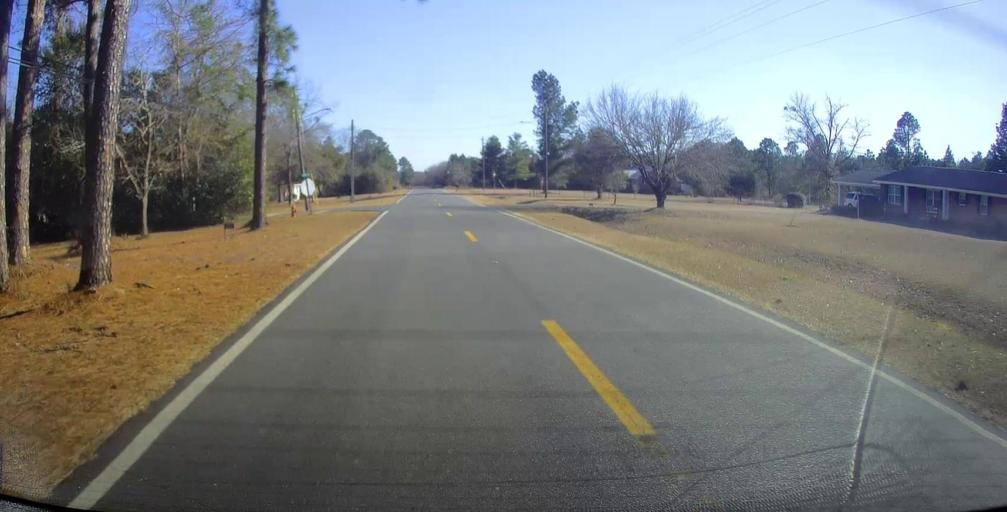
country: US
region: Georgia
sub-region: Taylor County
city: Butler
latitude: 32.5491
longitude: -84.2288
